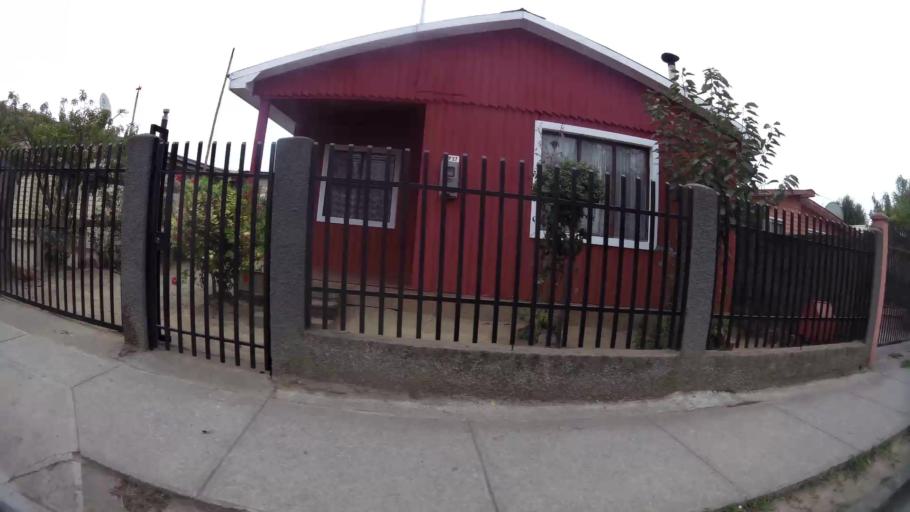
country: CL
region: Biobio
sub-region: Provincia de Concepcion
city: Concepcion
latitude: -36.8184
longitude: -72.9872
